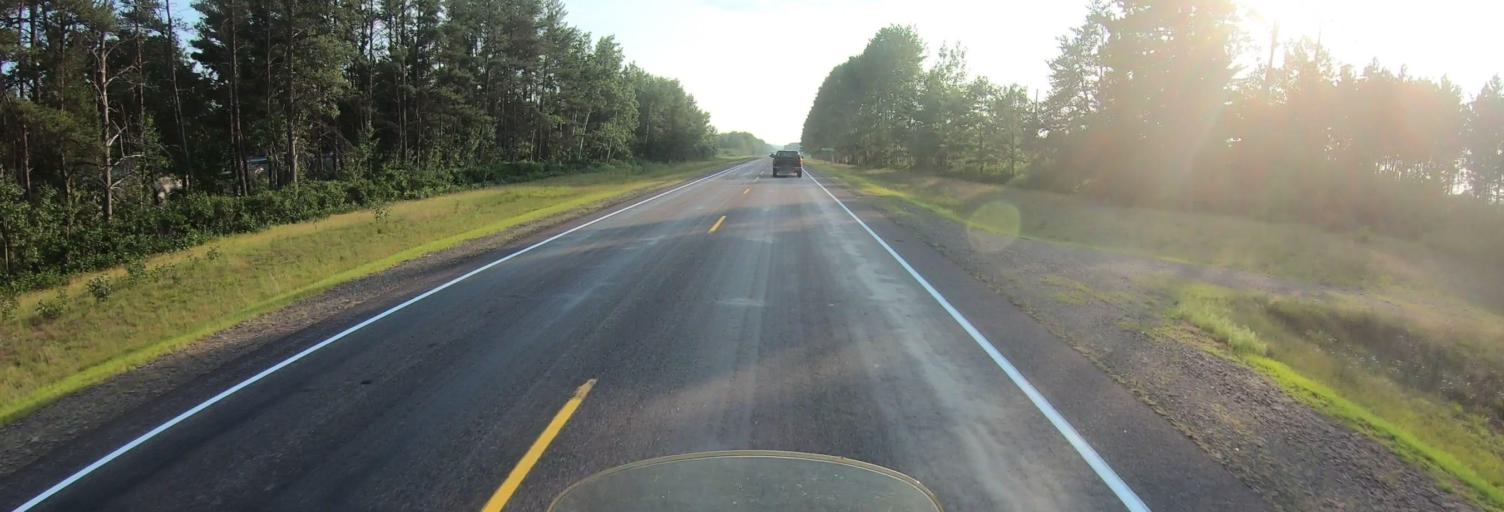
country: US
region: Wisconsin
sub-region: Washburn County
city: Spooner
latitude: 45.9180
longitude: -91.7396
